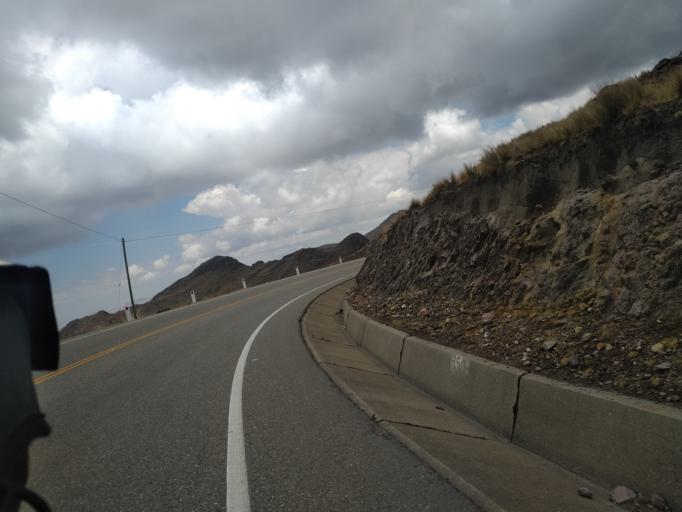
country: PE
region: La Libertad
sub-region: Provincia de Santiago de Chuco
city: Quiruvilca
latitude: -7.9723
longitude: -78.2068
